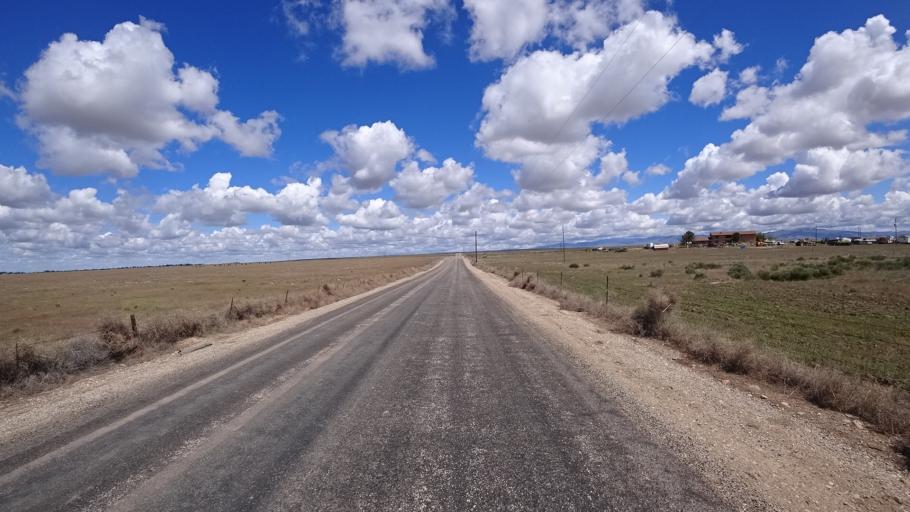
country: US
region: Idaho
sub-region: Ada County
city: Kuna
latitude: 43.4691
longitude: -116.2744
